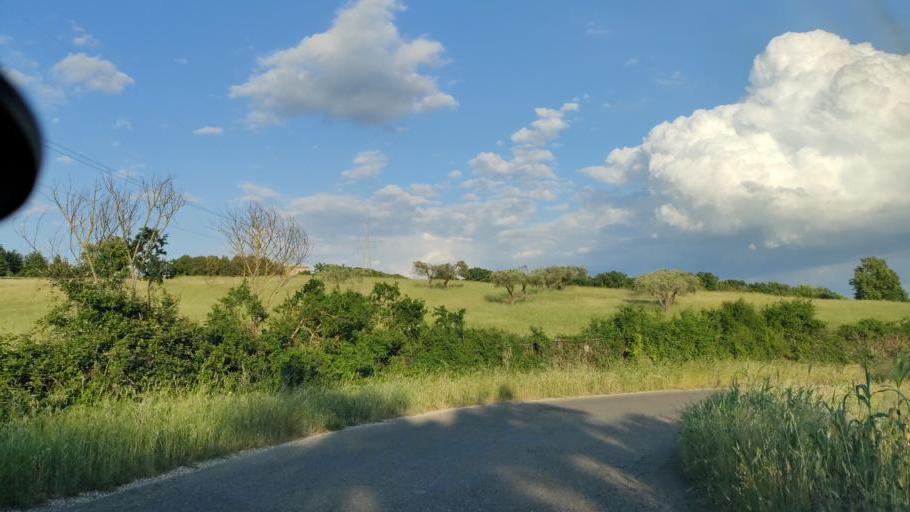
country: IT
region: Umbria
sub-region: Provincia di Terni
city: Amelia
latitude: 42.5818
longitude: 12.3901
